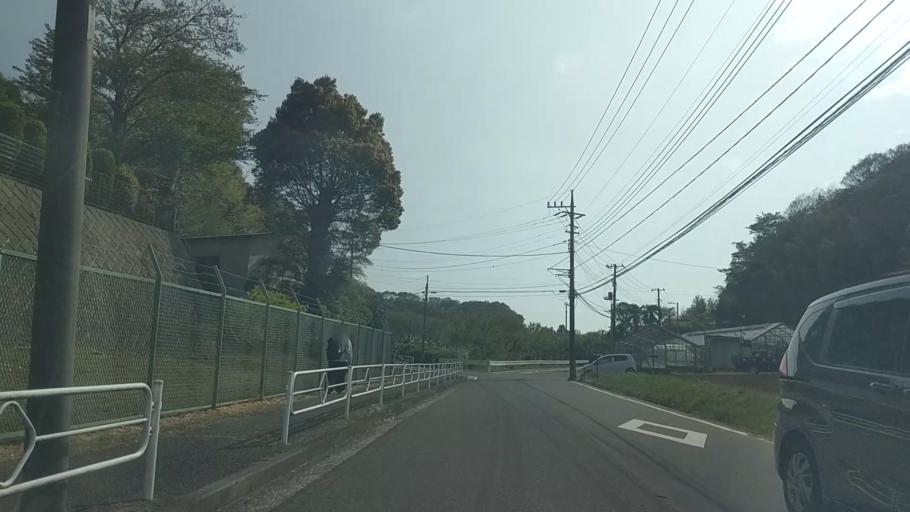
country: JP
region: Kanagawa
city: Kamakura
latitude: 35.3861
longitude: 139.5636
